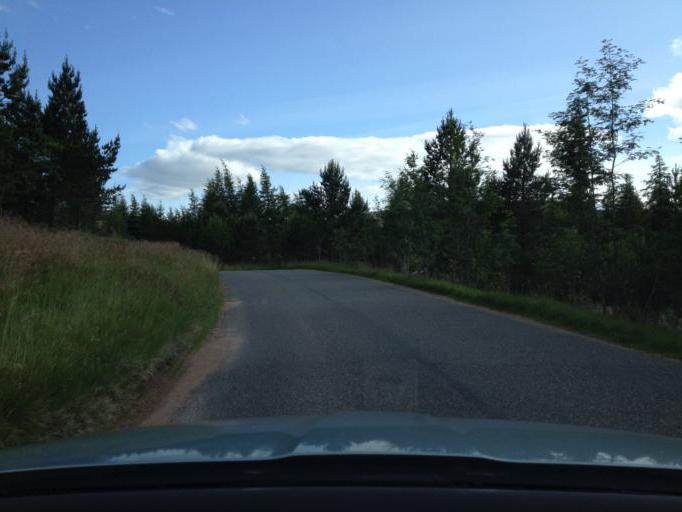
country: GB
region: Scotland
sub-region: Aberdeenshire
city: Banchory
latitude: 56.9528
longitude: -2.5857
